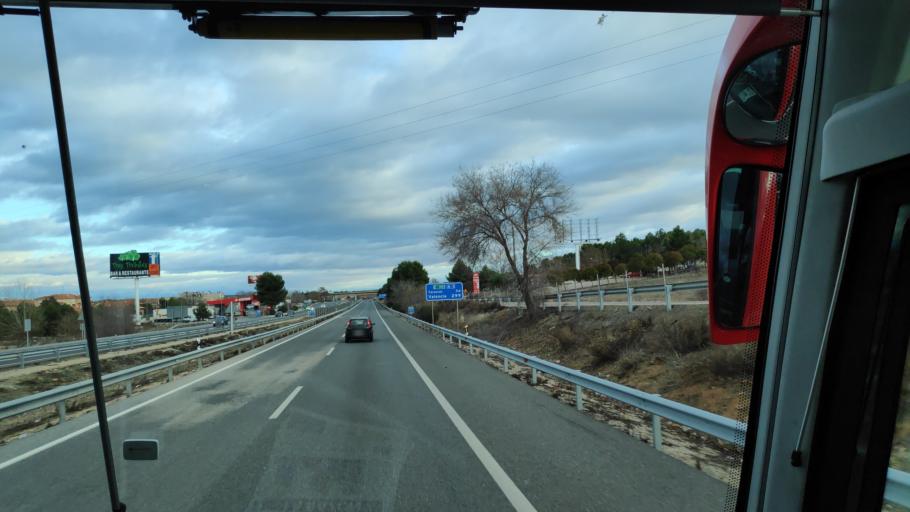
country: ES
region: Madrid
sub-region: Provincia de Madrid
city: Villarejo de Salvanes
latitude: 40.1685
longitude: -3.2881
